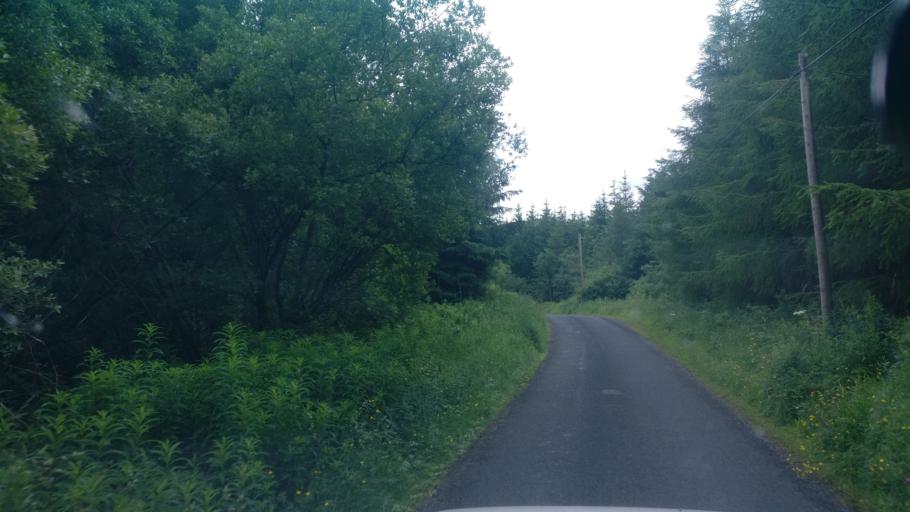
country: IE
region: Connaught
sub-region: County Galway
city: Loughrea
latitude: 53.1443
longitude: -8.5665
